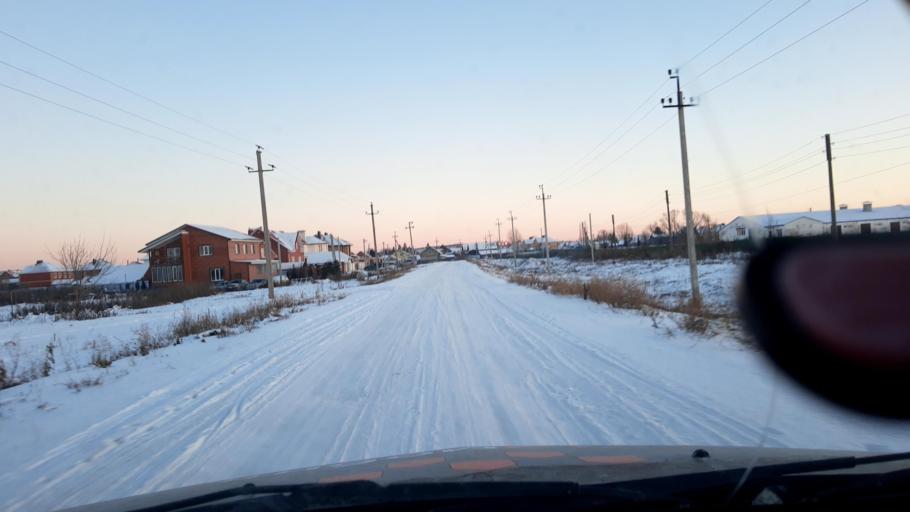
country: RU
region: Bashkortostan
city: Ufa
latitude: 54.6226
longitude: 55.8998
